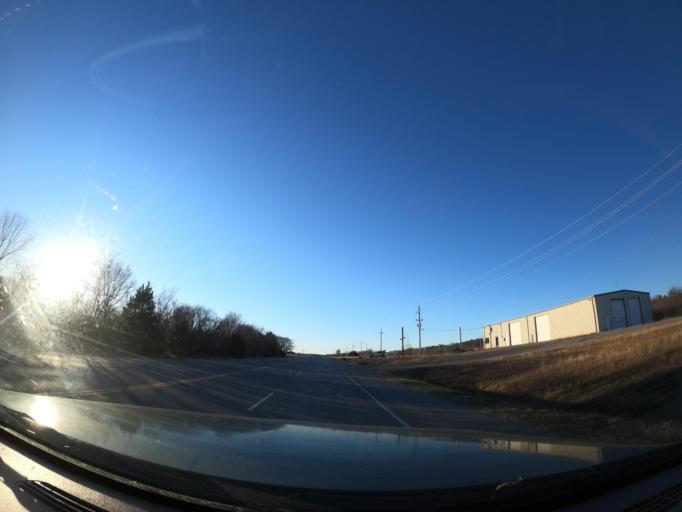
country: US
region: Oklahoma
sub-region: Pittsburg County
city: Krebs
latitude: 34.8976
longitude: -95.6786
